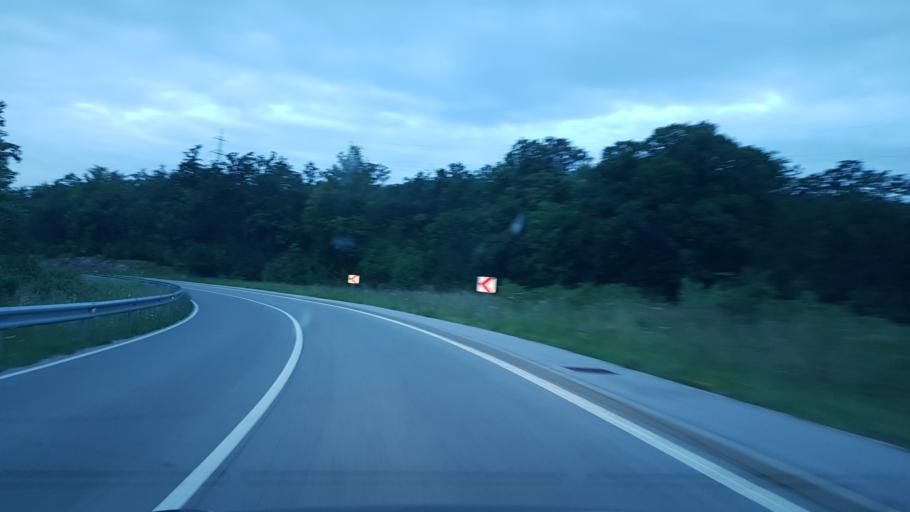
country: SI
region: Divaca
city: Divaca
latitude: 45.6792
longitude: 13.9562
